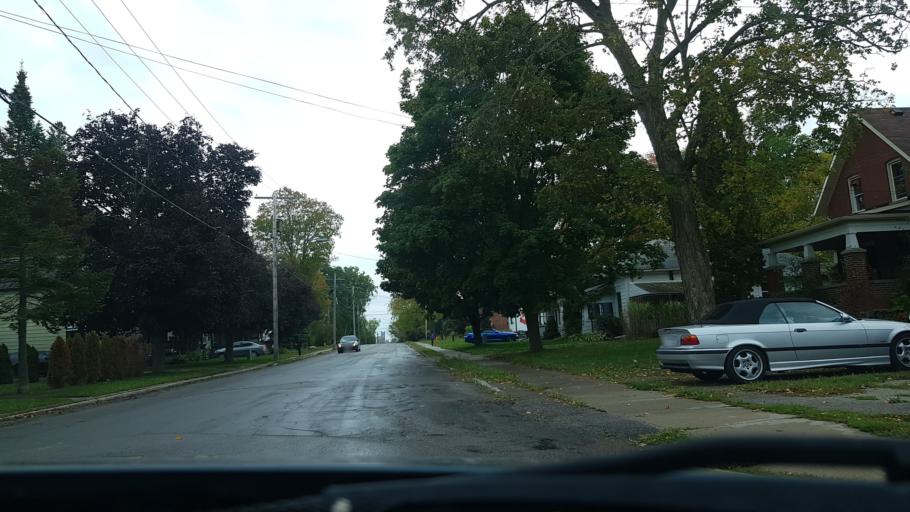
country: CA
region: Ontario
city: Omemee
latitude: 44.3644
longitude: -78.7414
